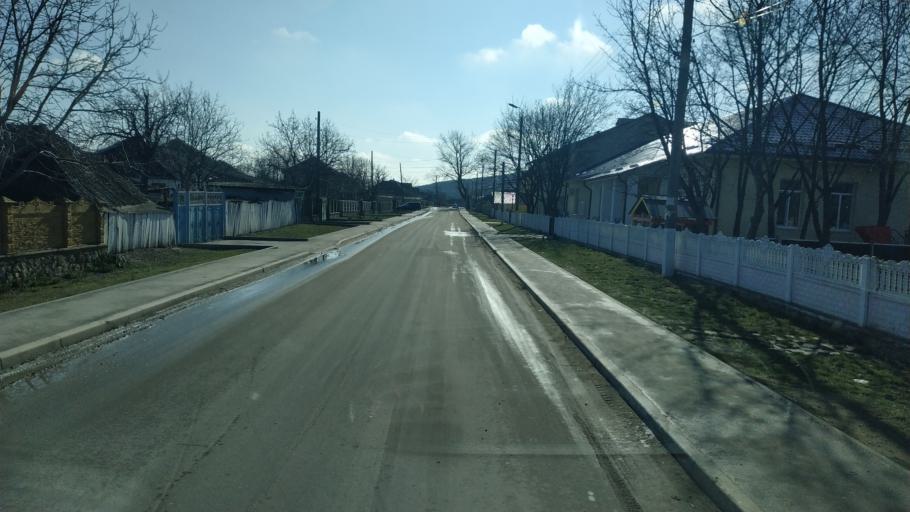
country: MD
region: Hincesti
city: Hincesti
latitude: 46.9272
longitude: 28.6531
